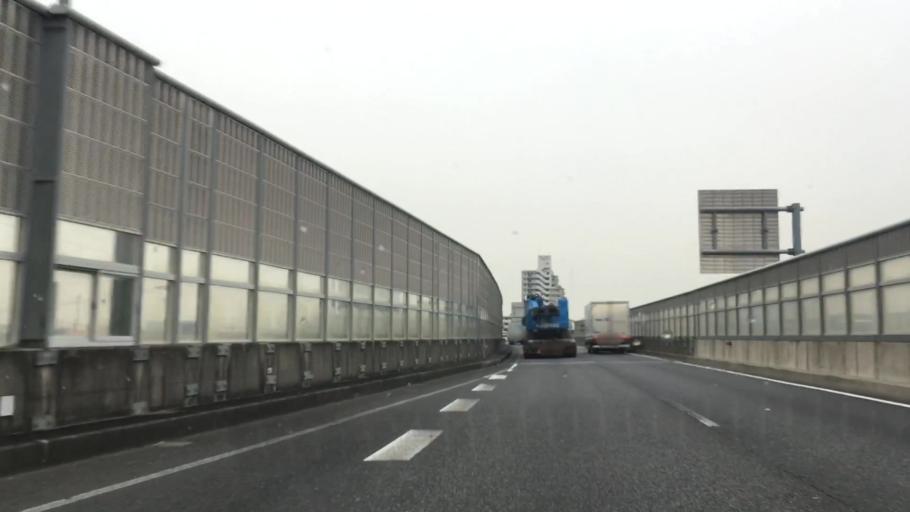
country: JP
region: Aichi
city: Chiryu
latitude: 34.9743
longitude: 137.0349
